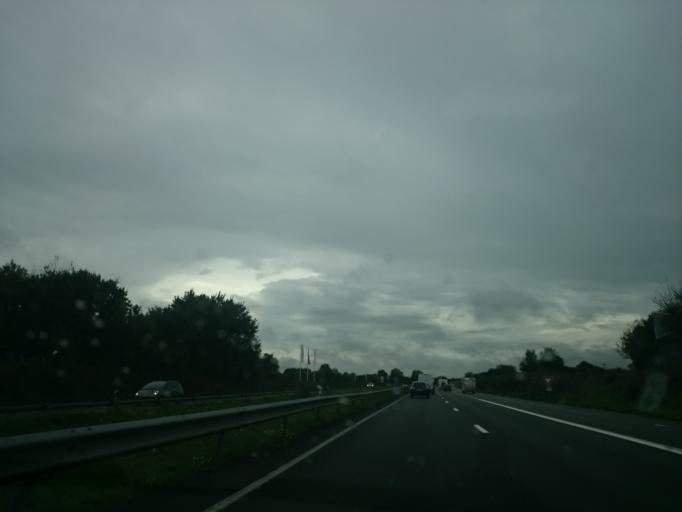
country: FR
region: Pays de la Loire
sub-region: Departement de la Loire-Atlantique
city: Vigneux-de-Bretagne
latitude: 47.2781
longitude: -1.7239
